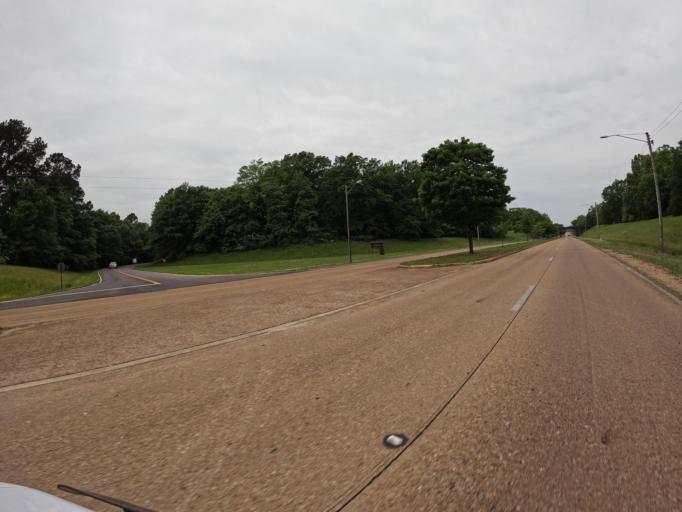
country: US
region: Mississippi
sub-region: Lee County
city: Tupelo
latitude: 34.2812
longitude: -88.7305
